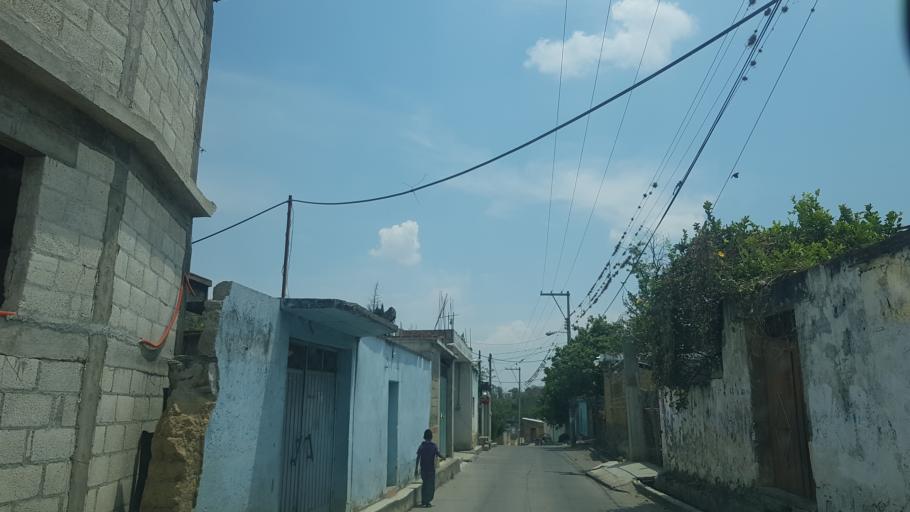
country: MX
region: Puebla
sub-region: Tochimilco
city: La Magdalena Yancuitlalpan
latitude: 18.8877
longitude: -98.6091
